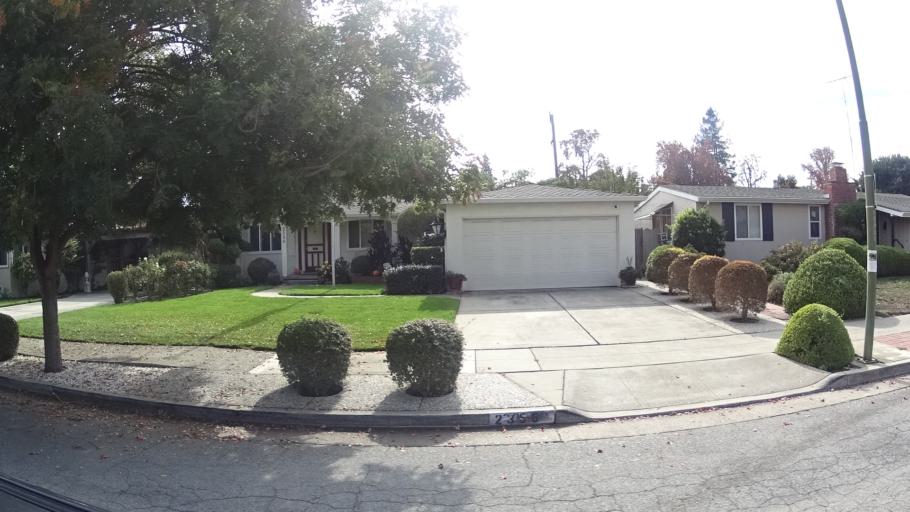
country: US
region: California
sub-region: Santa Clara County
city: Burbank
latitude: 37.3341
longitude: -121.9458
